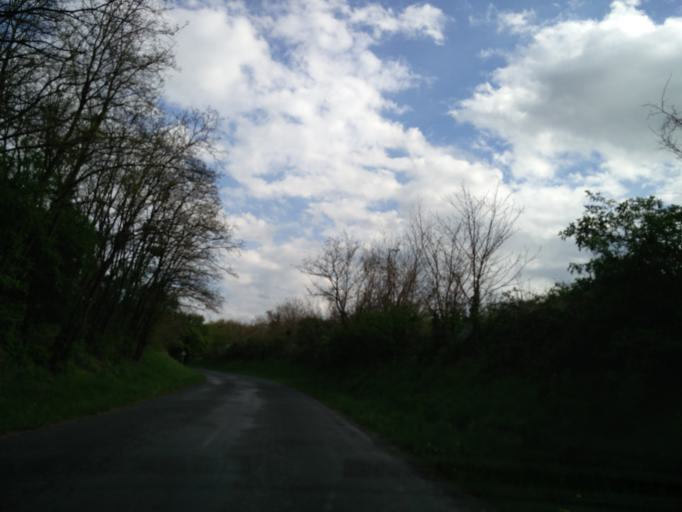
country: HU
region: Zala
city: Zalaegerszeg
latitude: 46.8771
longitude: 16.9209
